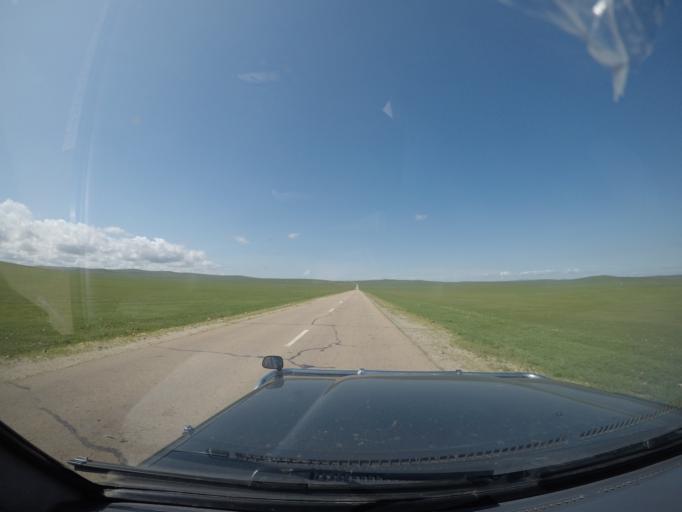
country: MN
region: Hentiy
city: Bayan
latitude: 47.2870
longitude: 111.0272
